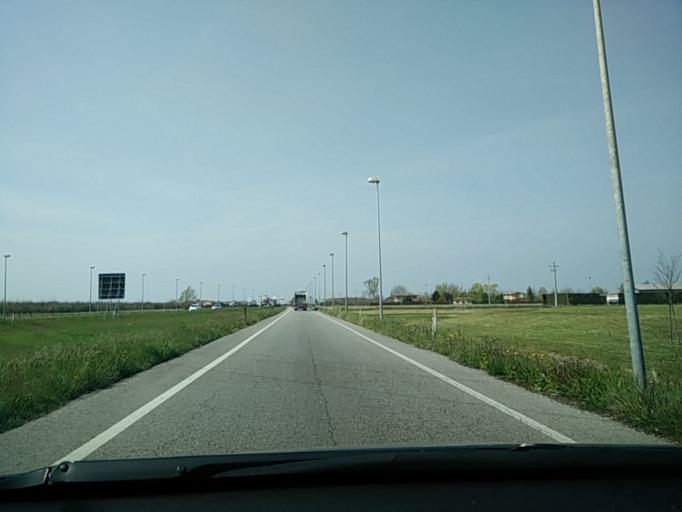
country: IT
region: Veneto
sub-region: Provincia di Venezia
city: San Dona di Piave
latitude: 45.6452
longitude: 12.5936
